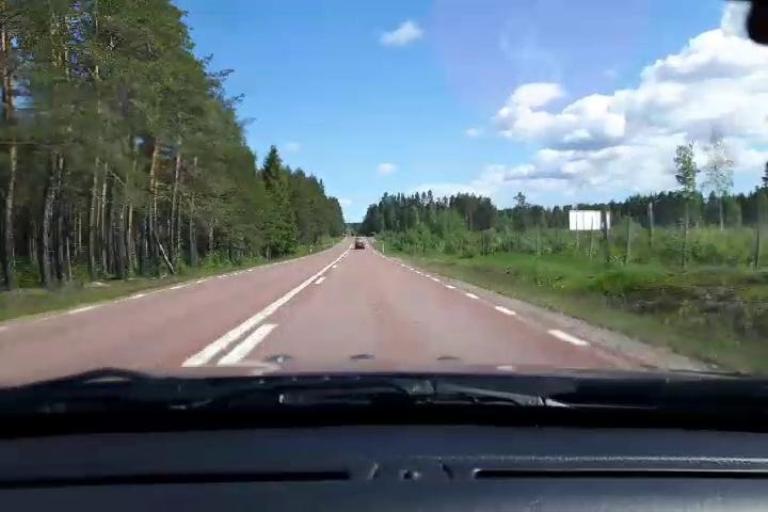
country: SE
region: Gaevleborg
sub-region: Hudiksvalls Kommun
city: Delsbo
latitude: 61.7891
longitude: 16.6008
